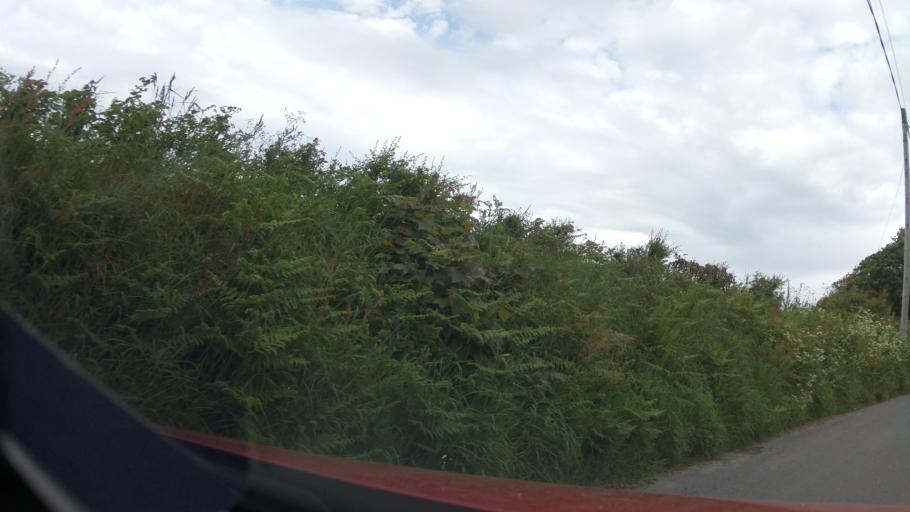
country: GB
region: England
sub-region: Devon
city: Dartmouth
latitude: 50.3512
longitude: -3.6607
